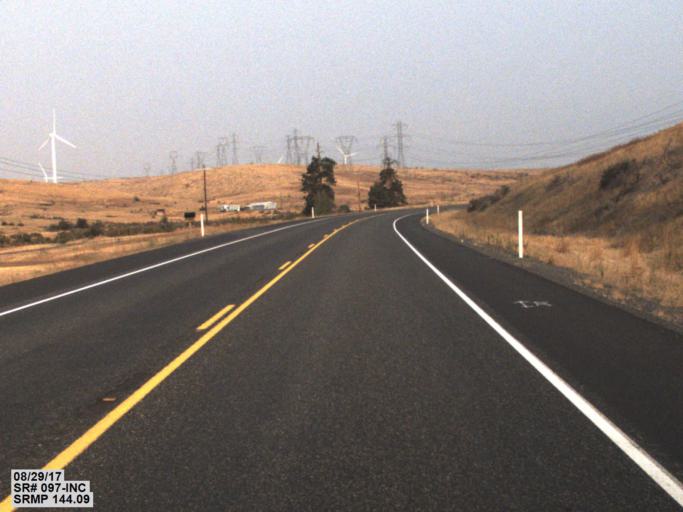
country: US
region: Washington
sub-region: Kittitas County
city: Ellensburg
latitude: 47.1275
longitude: -120.6814
